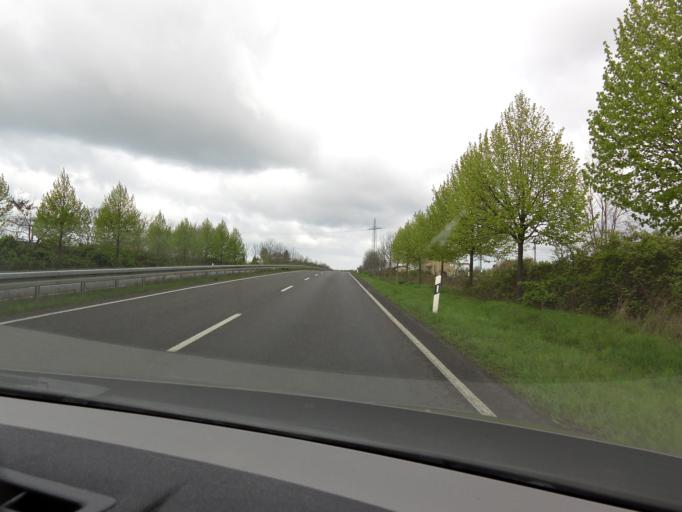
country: DE
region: Saxony
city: Leipzig
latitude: 51.3824
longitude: 12.3146
